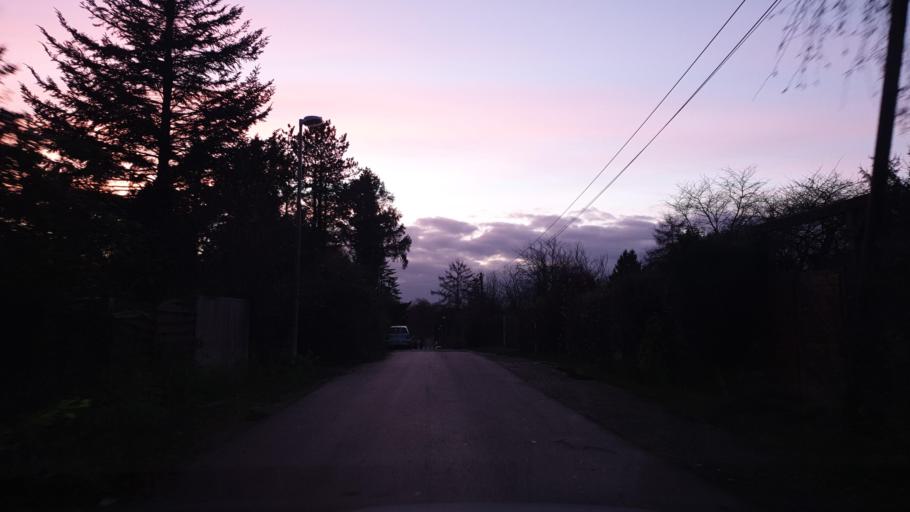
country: DE
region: Lower Saxony
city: Osnabrueck
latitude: 52.2589
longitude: 8.0379
